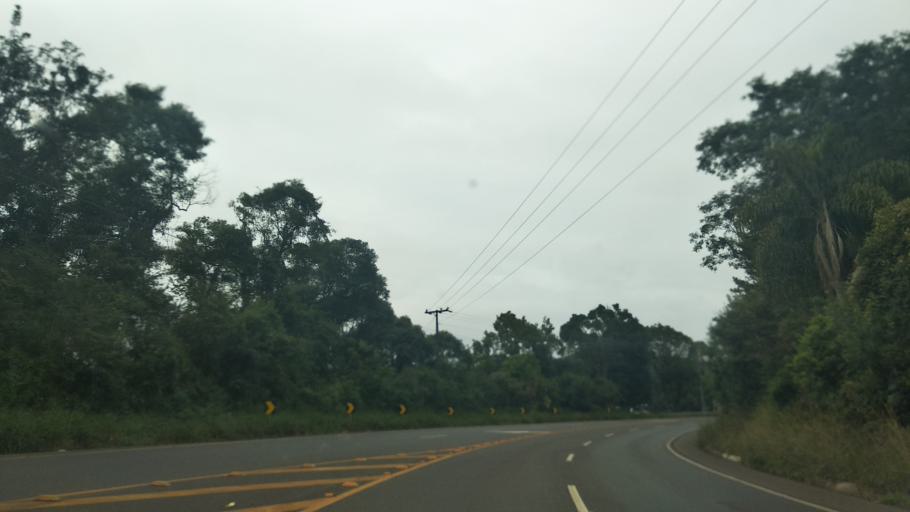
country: BR
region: Santa Catarina
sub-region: Videira
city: Videira
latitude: -27.0764
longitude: -51.2338
